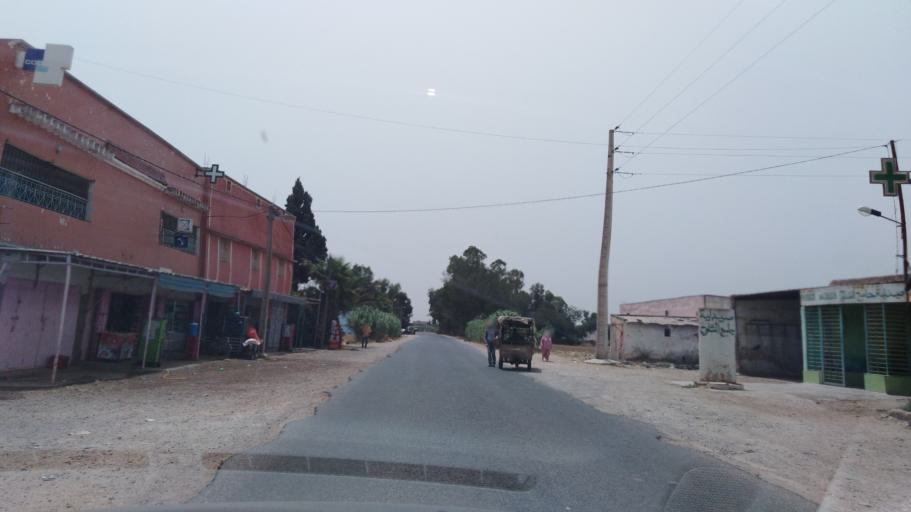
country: MA
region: Grand Casablanca
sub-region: Mediouna
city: Mediouna
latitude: 33.3999
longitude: -7.5117
